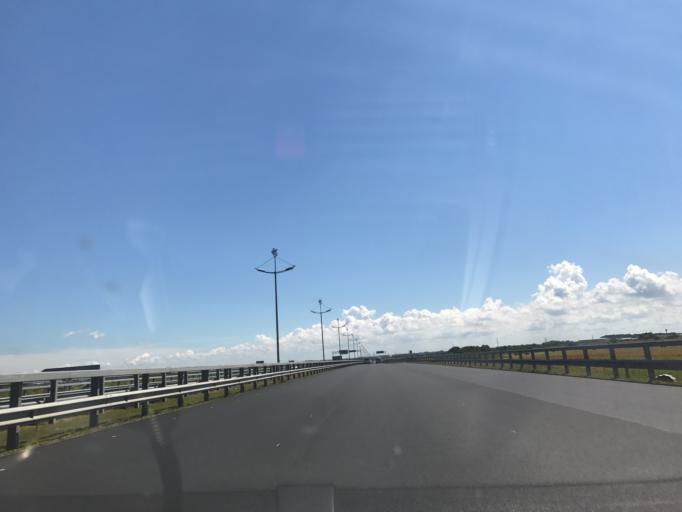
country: RU
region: Kaliningrad
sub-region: Zelenogradskiy Rayon
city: Zelenogradsk
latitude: 54.9067
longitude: 20.5026
